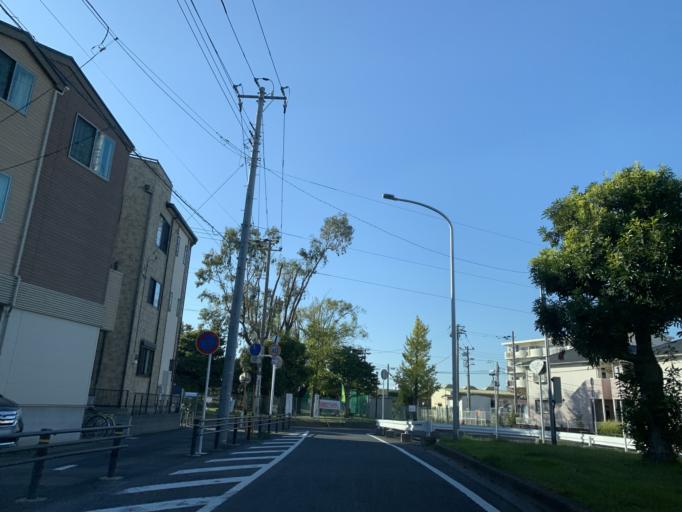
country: JP
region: Tokyo
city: Urayasu
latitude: 35.6578
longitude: 139.8894
